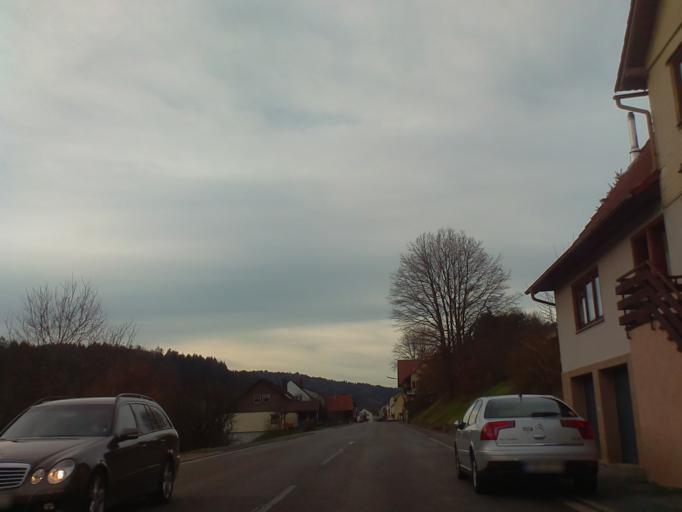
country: DE
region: Hesse
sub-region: Regierungsbezirk Darmstadt
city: Erbach
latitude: 49.6372
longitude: 8.9088
